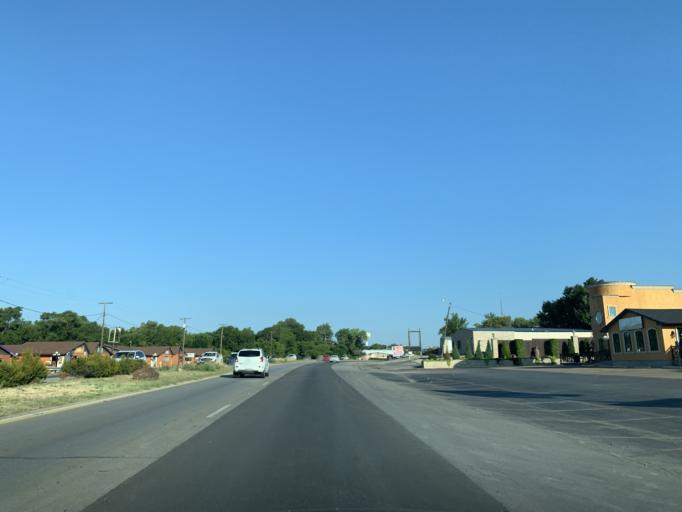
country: US
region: Texas
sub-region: Tarrant County
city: Sansom Park
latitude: 32.7975
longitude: -97.4024
